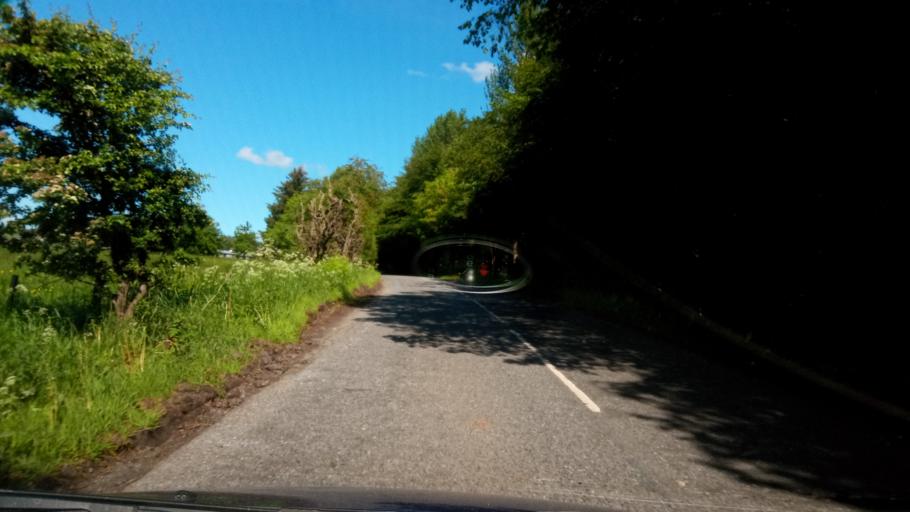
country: GB
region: Scotland
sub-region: The Scottish Borders
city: Jedburgh
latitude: 55.3885
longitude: -2.6229
